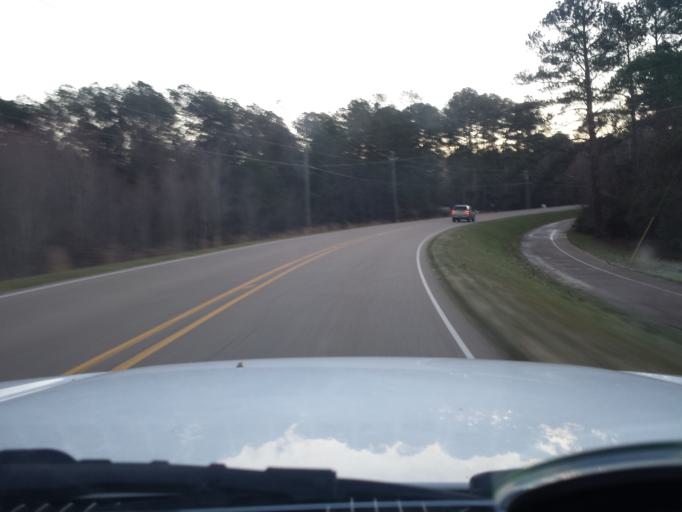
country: US
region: Mississippi
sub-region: Madison County
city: Madison
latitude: 32.4134
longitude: -90.0102
